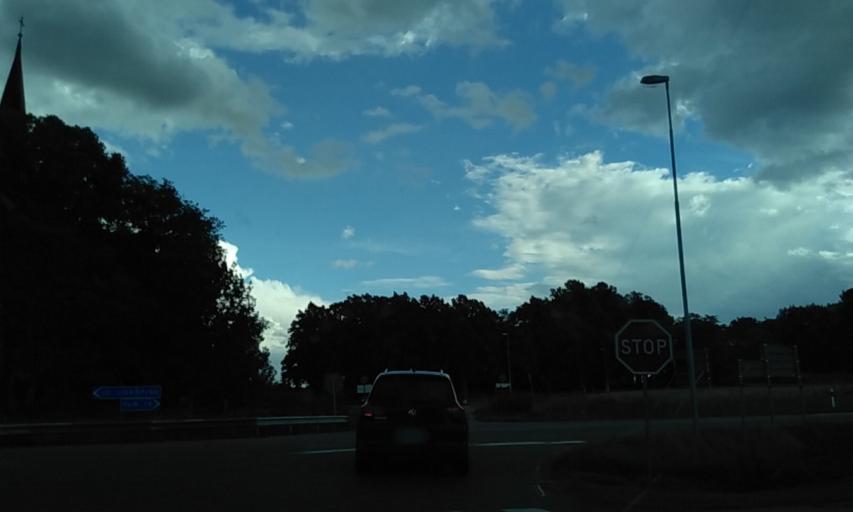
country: SE
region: Vaestra Goetaland
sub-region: Lidkopings Kommun
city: Lidkoping
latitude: 58.5080
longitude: 13.0056
